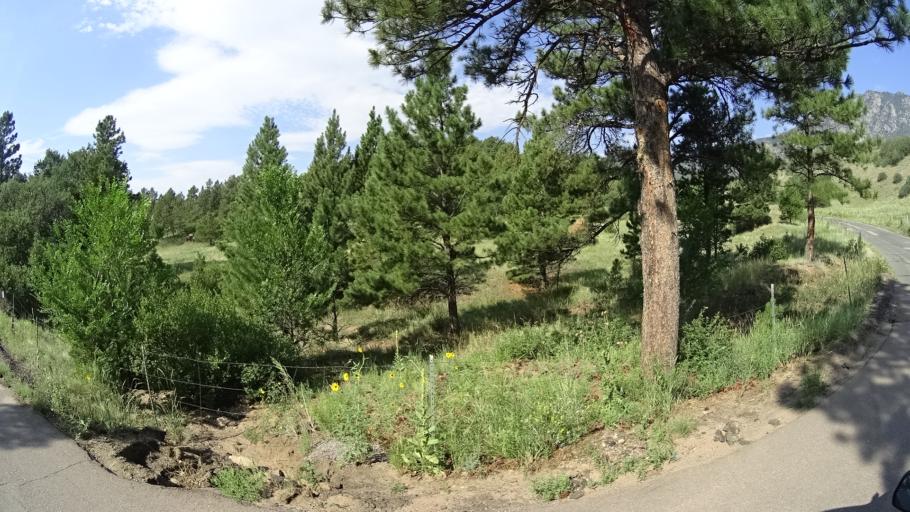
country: US
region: Colorado
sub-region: El Paso County
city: Fort Carson
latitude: 38.7202
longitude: -104.8251
